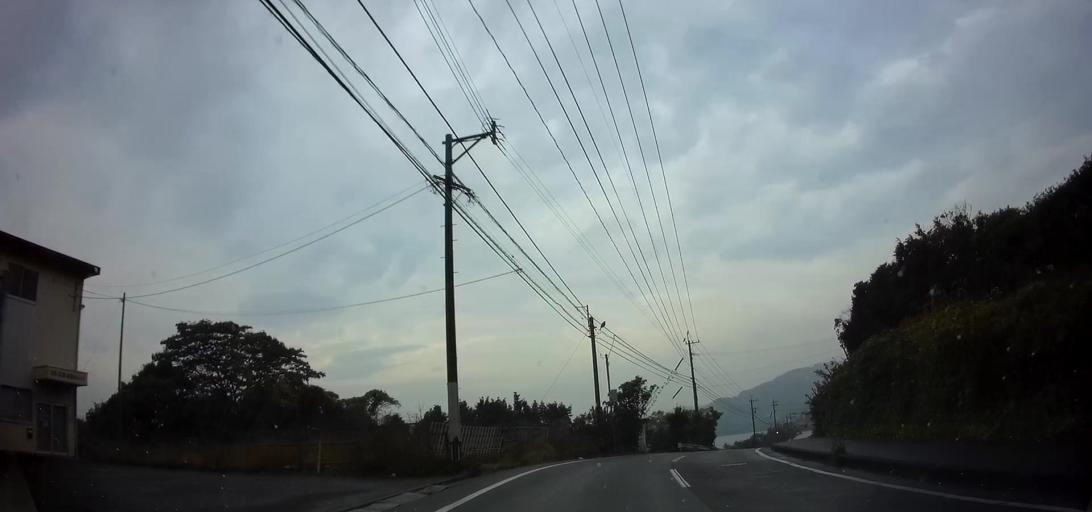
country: JP
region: Nagasaki
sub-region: Isahaya-shi
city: Isahaya
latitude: 32.8496
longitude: 129.9945
